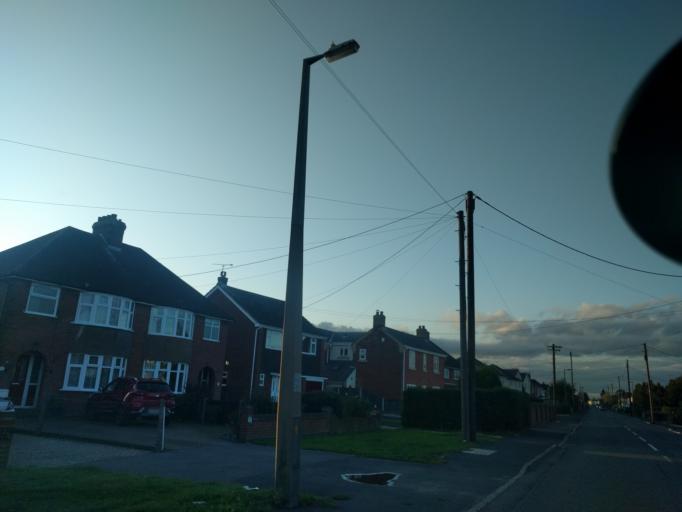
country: GB
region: England
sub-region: Essex
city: Rayne
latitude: 51.8723
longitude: 0.5790
